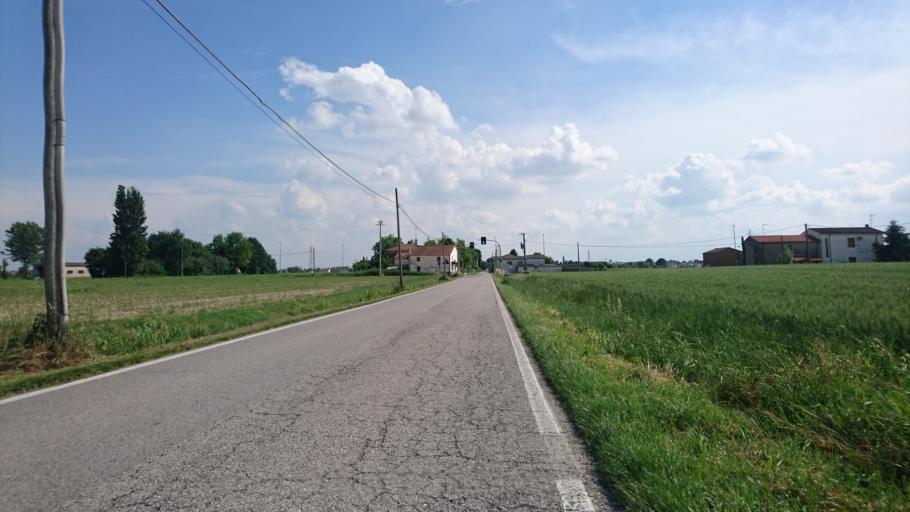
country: IT
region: Veneto
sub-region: Provincia di Rovigo
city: Castelmassa
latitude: 45.0352
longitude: 11.3132
